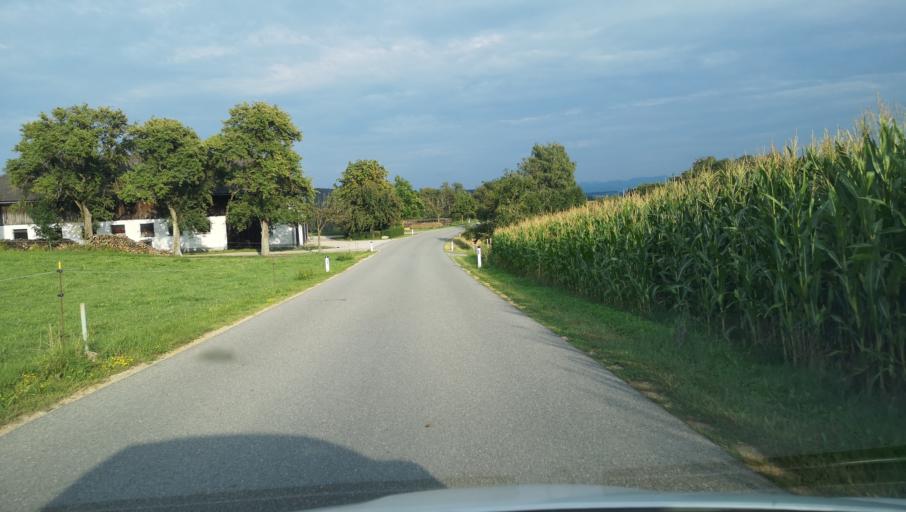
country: AT
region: Lower Austria
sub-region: Politischer Bezirk Amstetten
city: Sankt Georgen am Ybbsfelde
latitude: 48.1471
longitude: 14.9595
